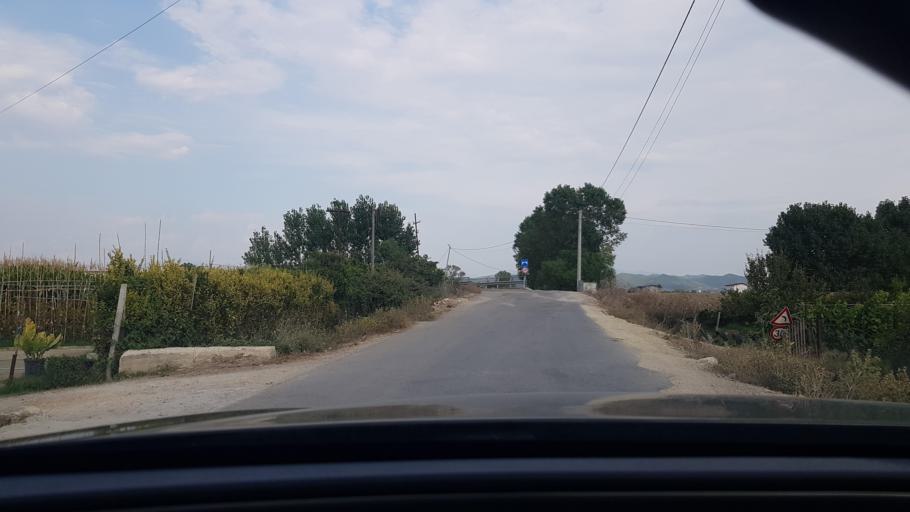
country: AL
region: Durres
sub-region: Rrethi i Durresit
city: Katundi i Ri
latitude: 41.4852
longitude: 19.5251
